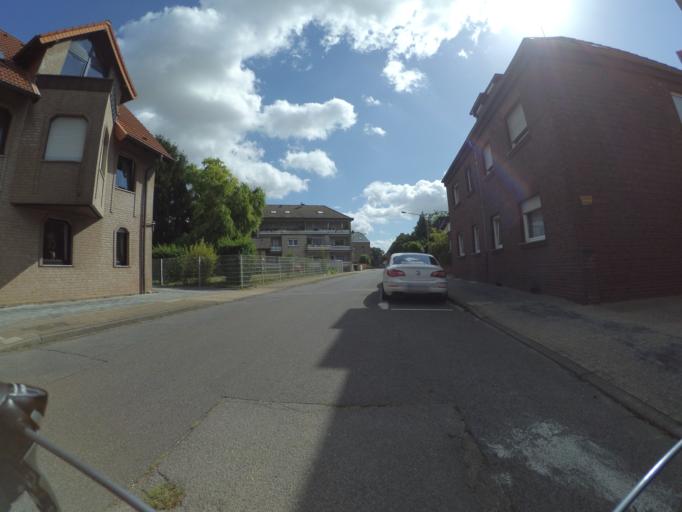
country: DE
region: North Rhine-Westphalia
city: Baesweiler
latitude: 50.8963
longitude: 6.1813
